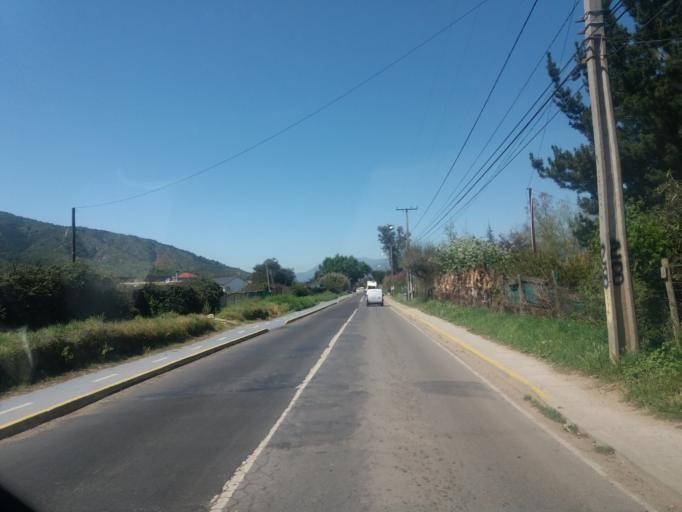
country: CL
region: Valparaiso
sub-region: Provincia de Marga Marga
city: Limache
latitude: -32.9771
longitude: -71.2894
